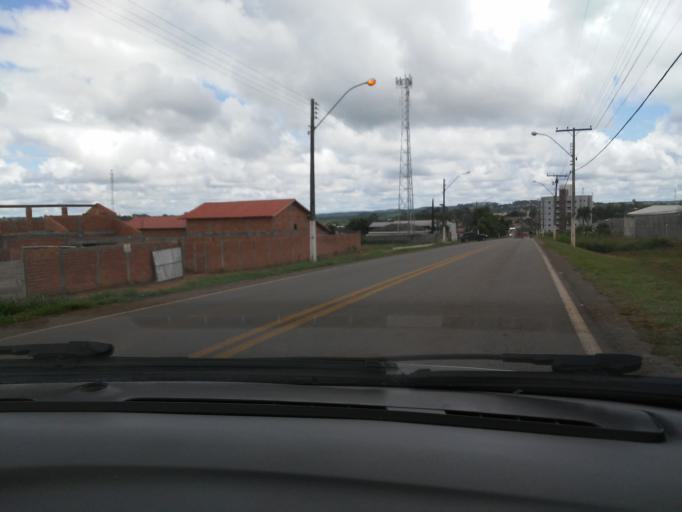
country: BR
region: Goias
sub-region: Ipameri
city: Ipameri
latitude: -17.7374
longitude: -48.1619
